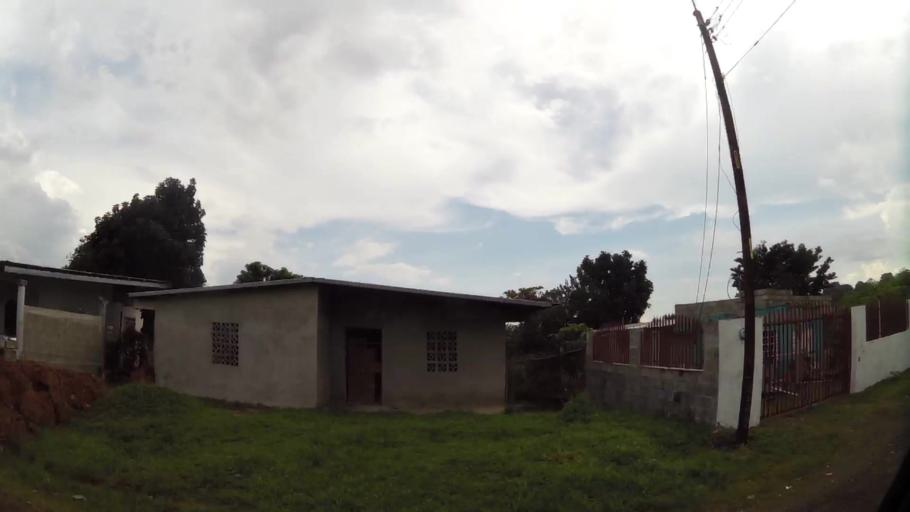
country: PA
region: Panama
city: Tocumen
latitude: 9.1121
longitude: -79.3778
